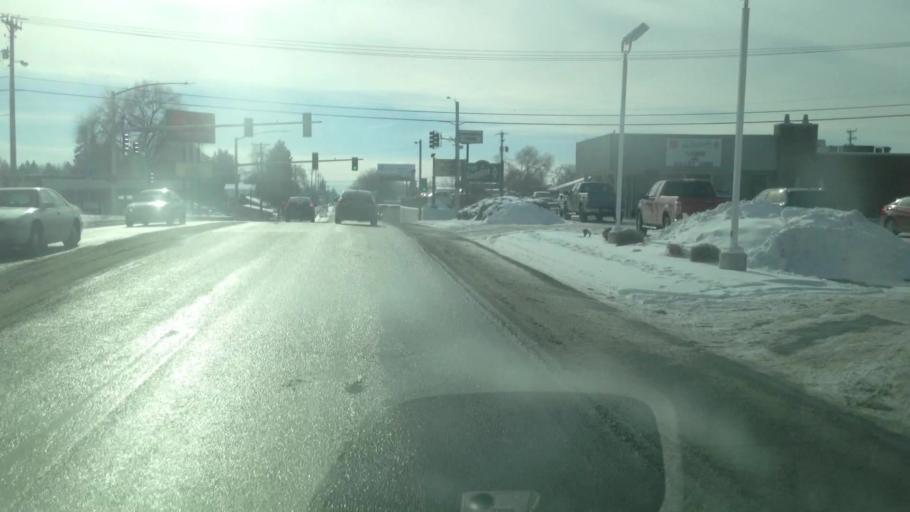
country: US
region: Idaho
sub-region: Bonneville County
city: Idaho Falls
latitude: 43.5048
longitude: -112.0239
